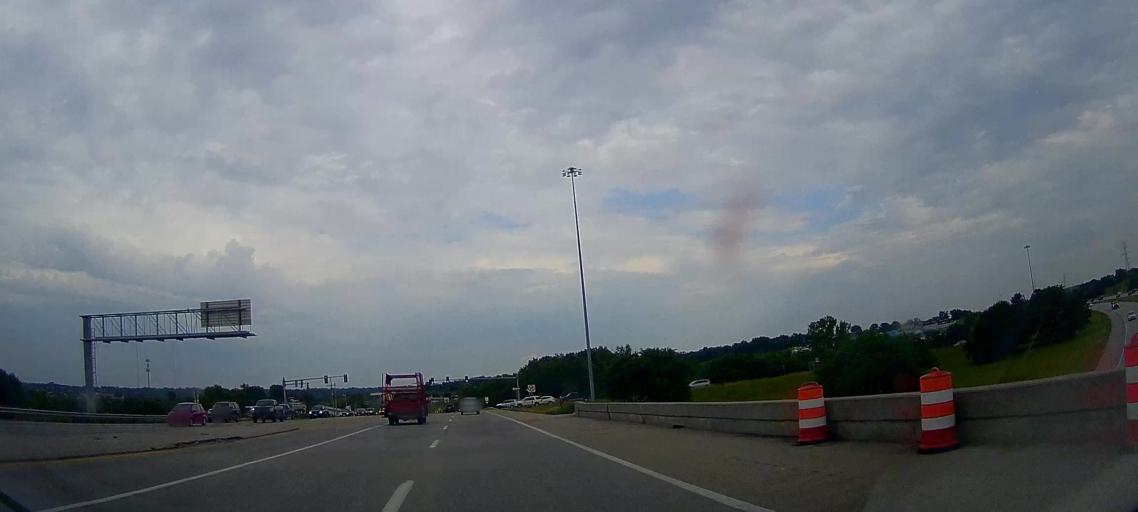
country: US
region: Nebraska
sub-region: Douglas County
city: Bennington
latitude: 41.3216
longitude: -96.0686
